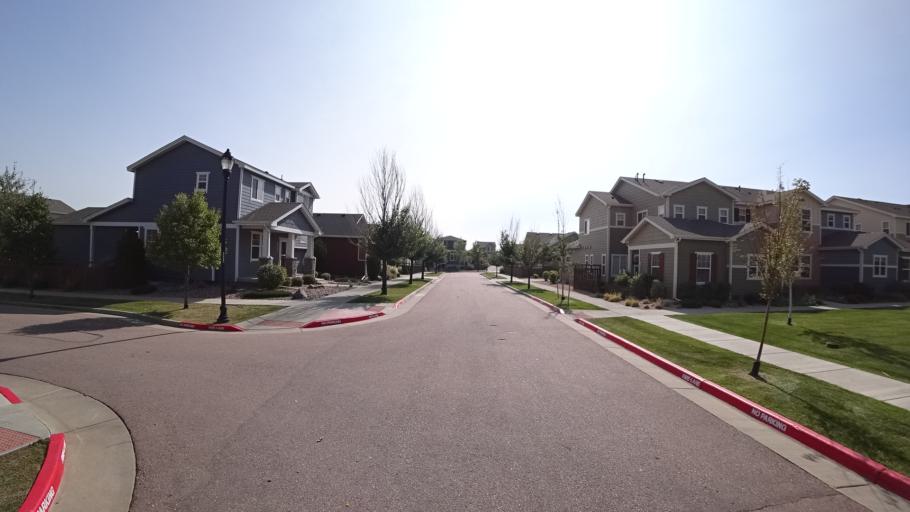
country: US
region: Colorado
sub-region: El Paso County
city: Colorado Springs
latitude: 38.8304
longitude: -104.8576
